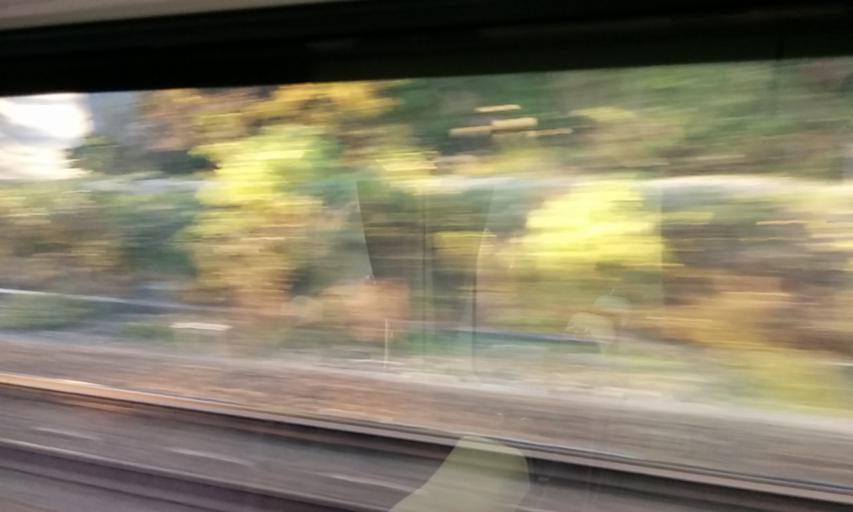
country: JP
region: Aichi
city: Seto
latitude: 35.2648
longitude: 137.0533
